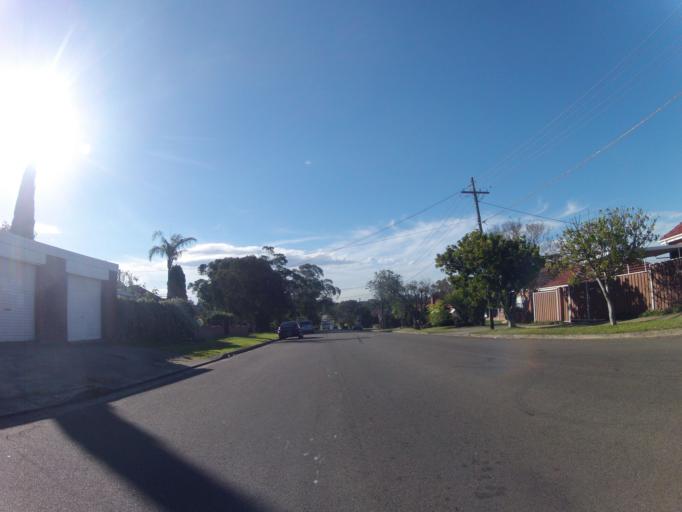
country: AU
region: New South Wales
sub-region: Canterbury
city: Roselands
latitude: -33.9458
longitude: 151.0807
